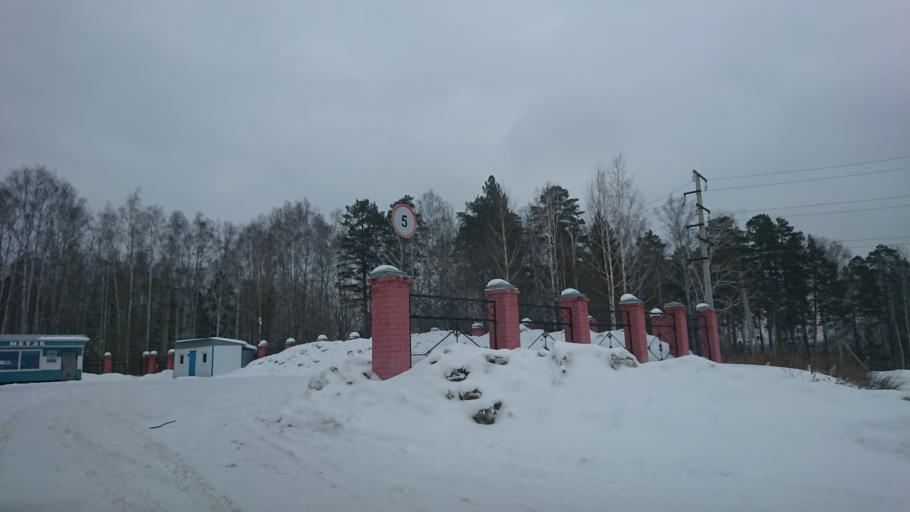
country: RU
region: Sverdlovsk
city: Sysert'
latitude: 56.4472
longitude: 60.8917
